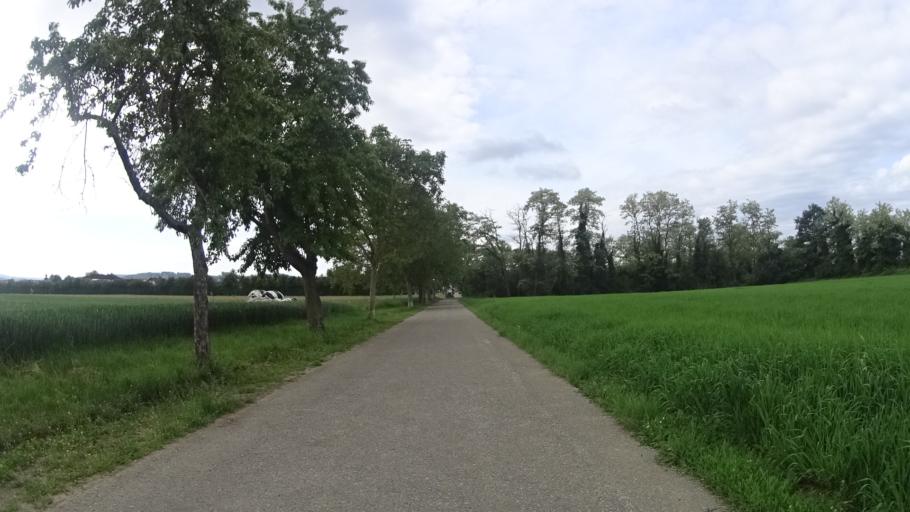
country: DE
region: Baden-Wuerttemberg
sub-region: Freiburg Region
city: Schliengen
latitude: 47.7749
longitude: 7.5529
